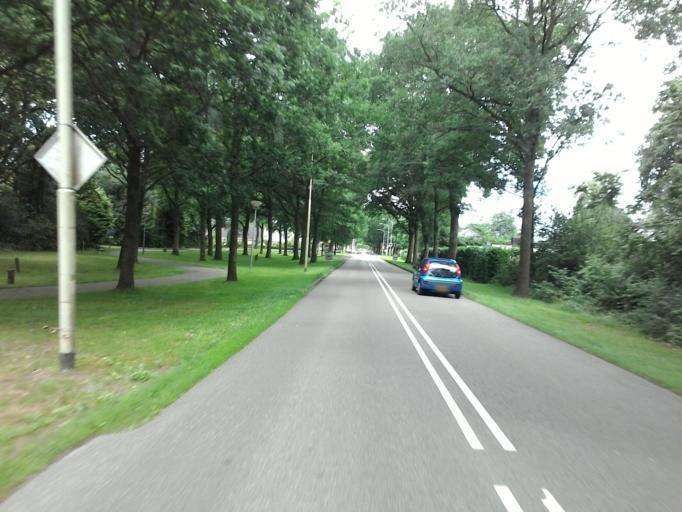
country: NL
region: Drenthe
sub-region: Gemeente Aa en Hunze
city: Anloo
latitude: 52.9803
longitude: 6.6493
